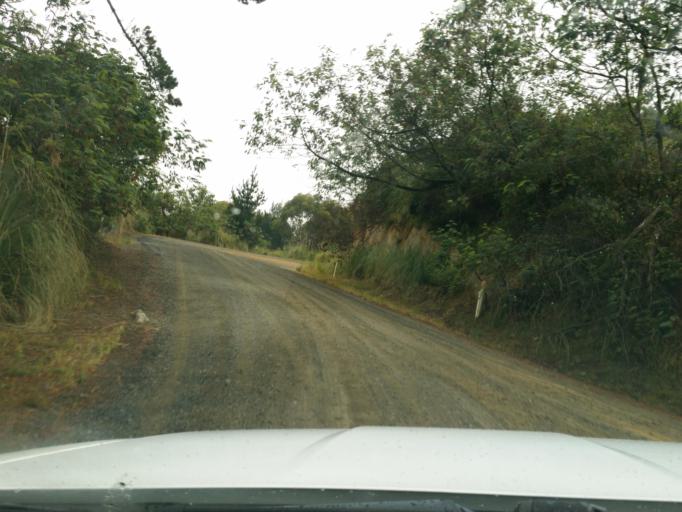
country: NZ
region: Northland
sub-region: Kaipara District
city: Dargaville
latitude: -36.0758
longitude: 173.8888
